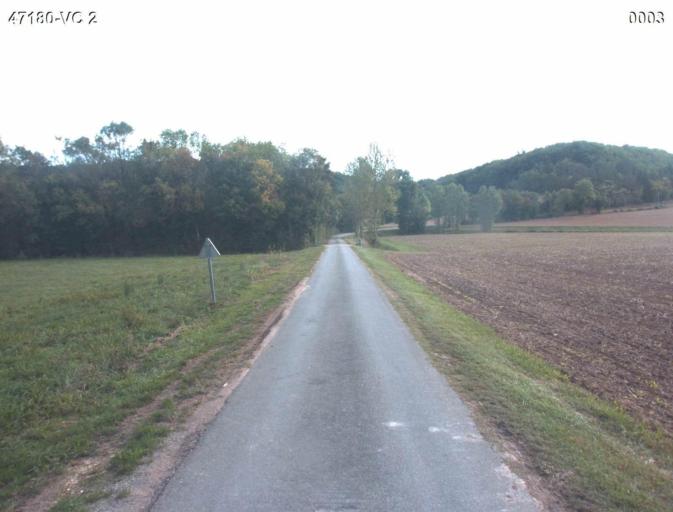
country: FR
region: Aquitaine
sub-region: Departement du Lot-et-Garonne
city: Nerac
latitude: 44.1676
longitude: 0.4213
